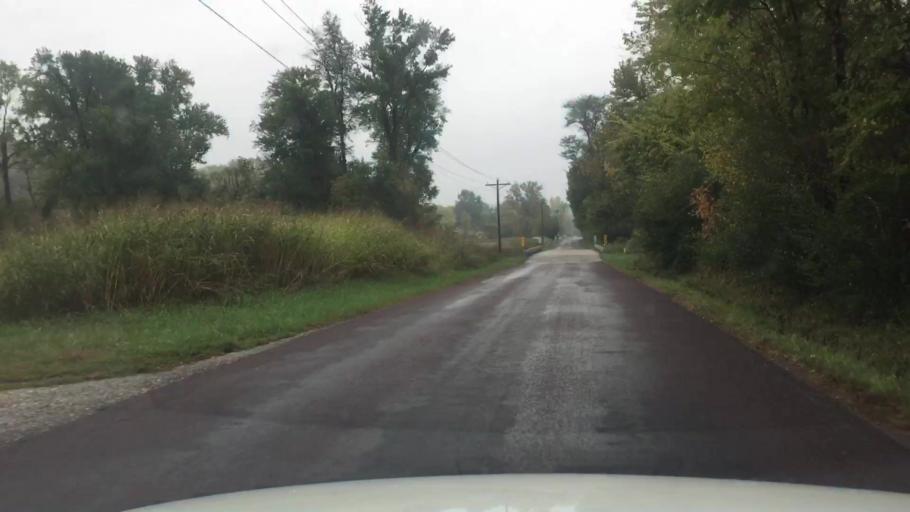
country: US
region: Missouri
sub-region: Boone County
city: Columbia
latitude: 38.8664
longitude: -92.3739
